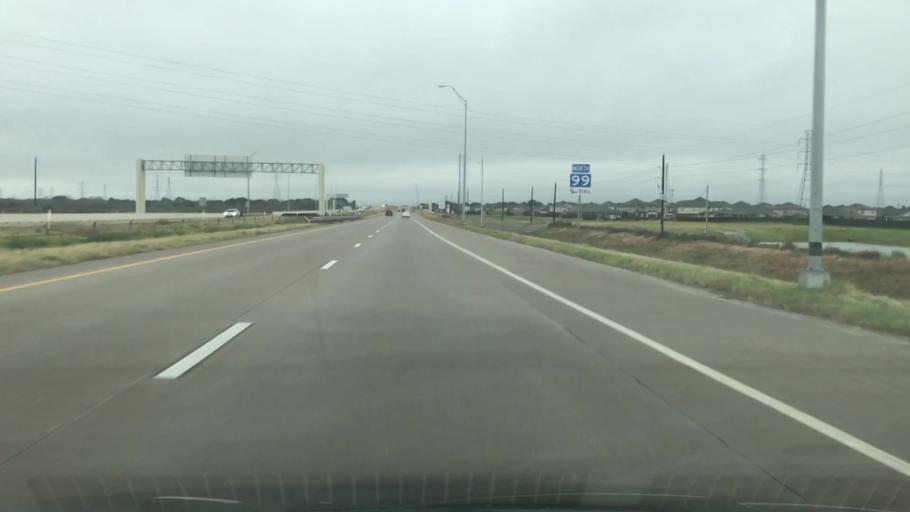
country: US
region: Texas
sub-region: Harris County
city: Katy
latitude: 29.8232
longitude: -95.7666
